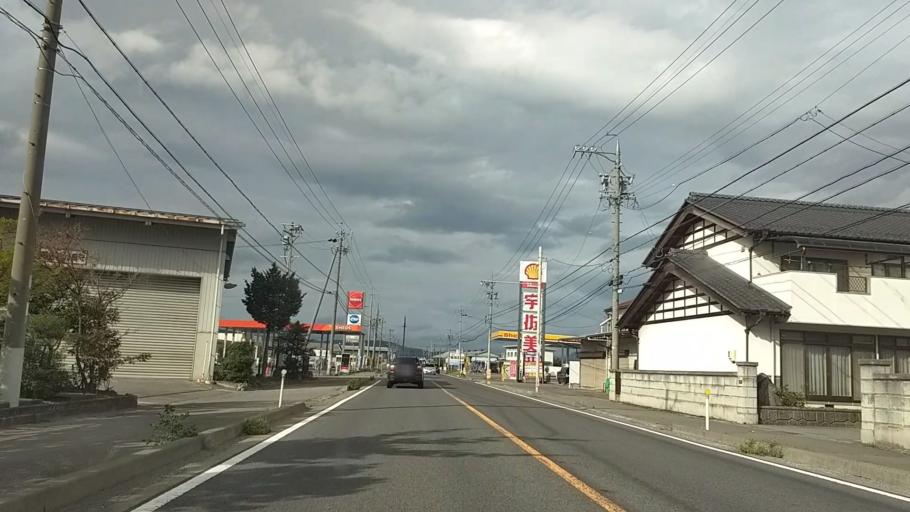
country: JP
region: Nagano
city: Suzaka
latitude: 36.6715
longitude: 138.2656
